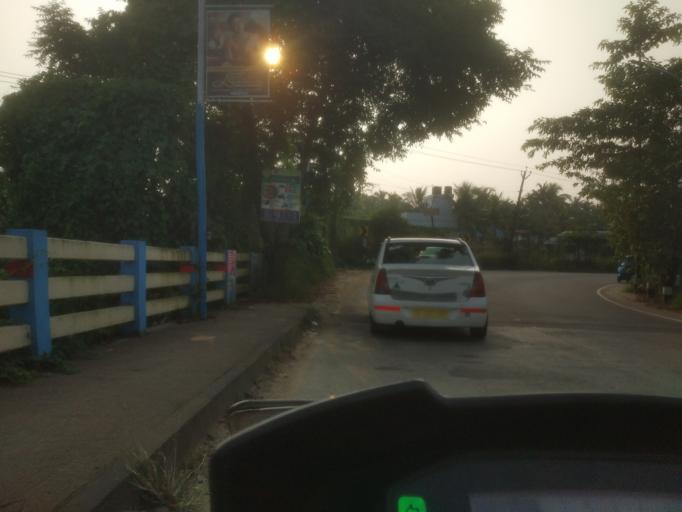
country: IN
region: Kerala
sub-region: Alappuzha
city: Arukutti
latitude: 9.9413
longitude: 76.3373
